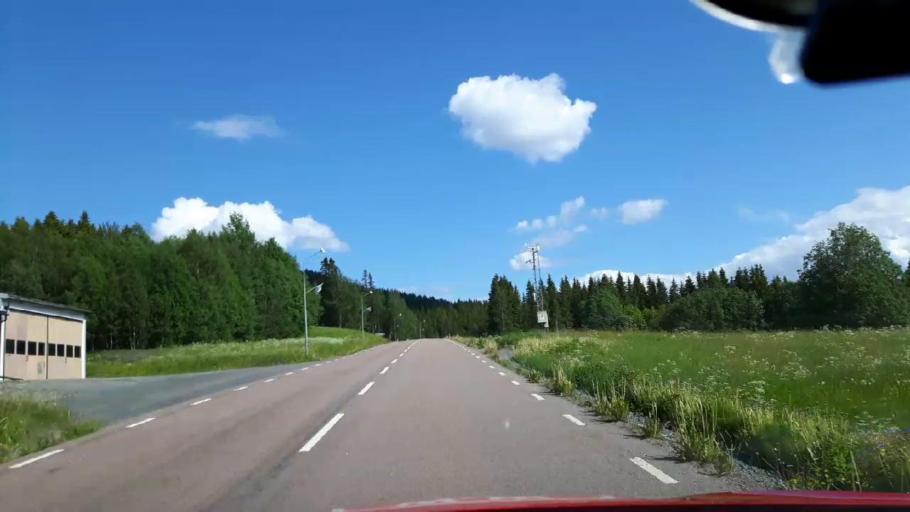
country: SE
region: Jaemtland
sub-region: Krokoms Kommun
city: Valla
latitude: 64.0657
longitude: 14.1445
